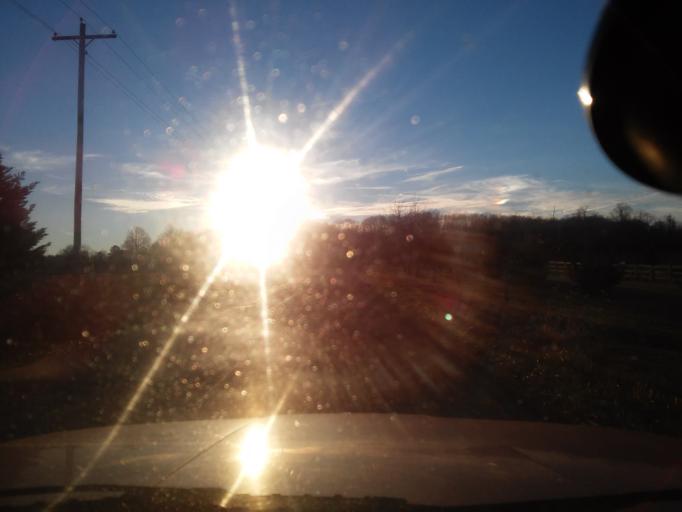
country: US
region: Virginia
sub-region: Goochland County
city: Goochland
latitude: 37.7123
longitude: -77.7581
